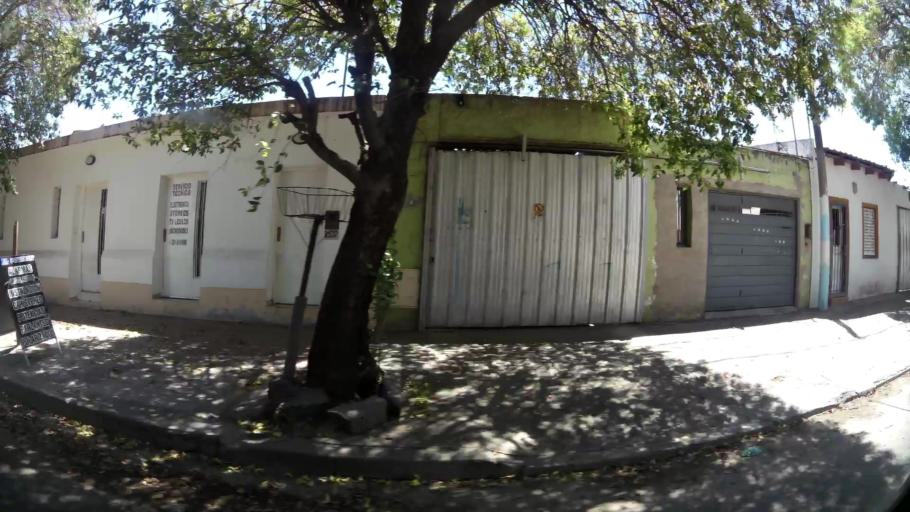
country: AR
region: Cordoba
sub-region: Departamento de Capital
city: Cordoba
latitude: -31.3803
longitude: -64.1466
